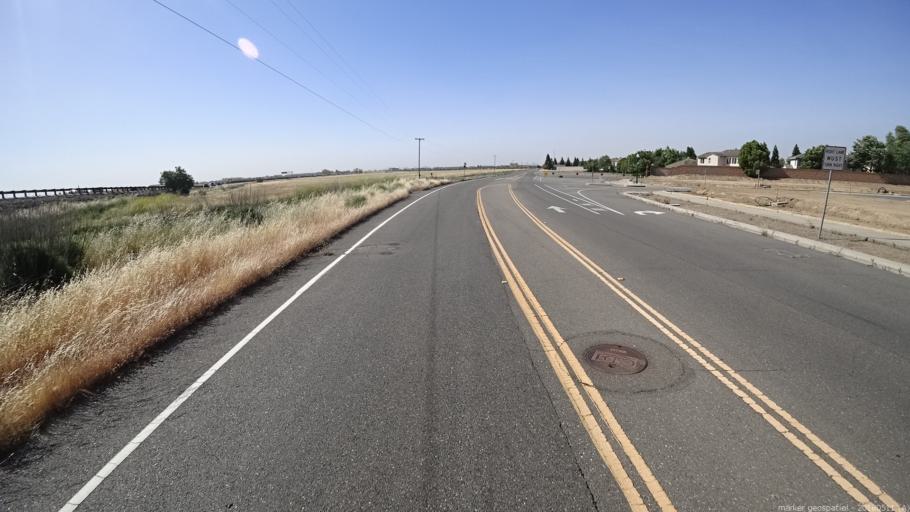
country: US
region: California
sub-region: Yolo County
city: West Sacramento
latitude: 38.6649
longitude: -121.5400
